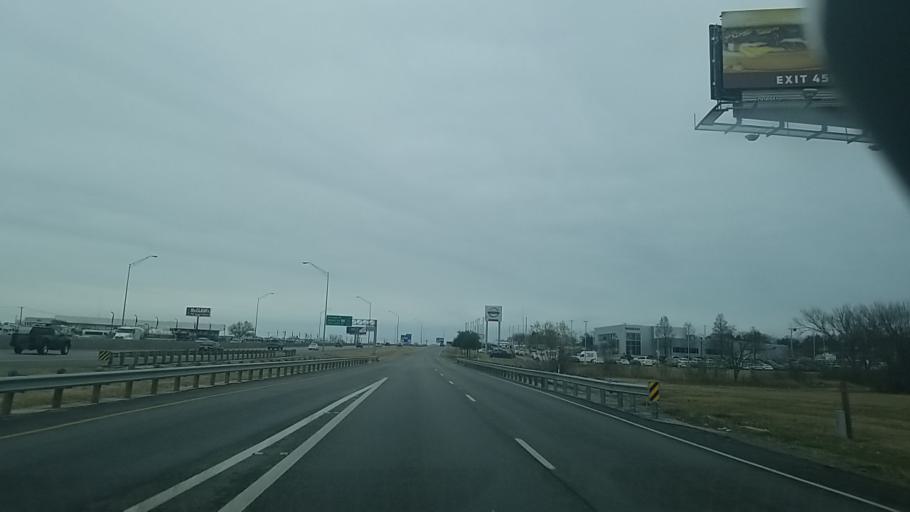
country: US
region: Texas
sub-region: Denton County
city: Corinth
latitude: 33.1587
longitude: -97.0688
